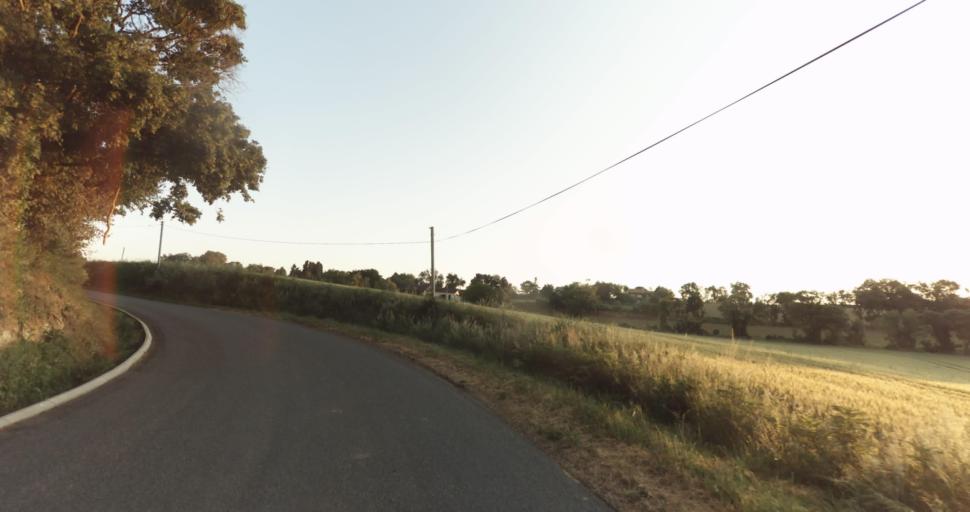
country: FR
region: Midi-Pyrenees
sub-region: Departement du Gers
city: Pujaudran
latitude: 43.6463
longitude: 1.1079
